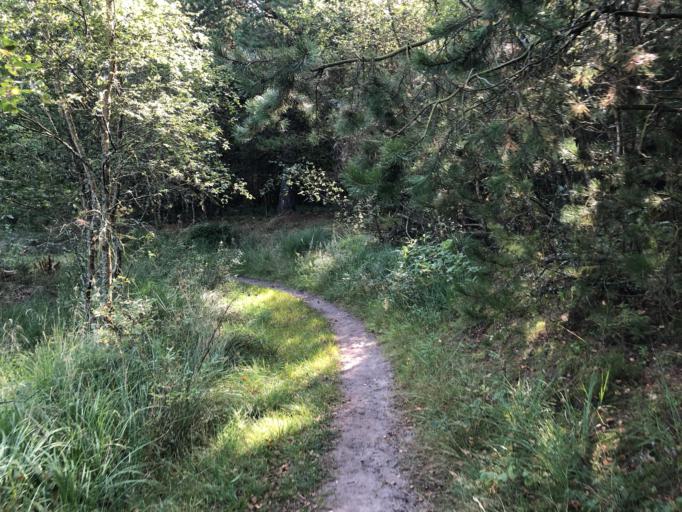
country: DK
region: Central Jutland
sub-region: Lemvig Kommune
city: Lemvig
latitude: 56.4768
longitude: 8.3352
